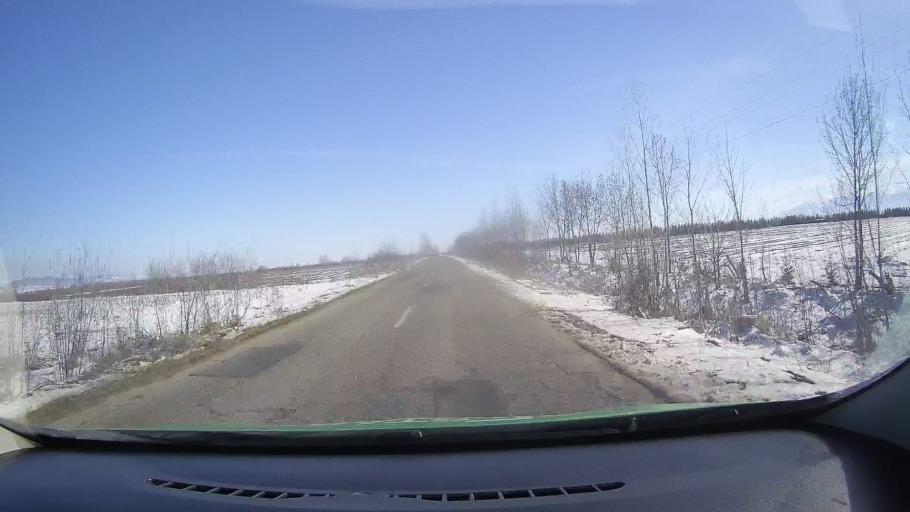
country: RO
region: Brasov
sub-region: Comuna Dragus
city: Dragus
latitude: 45.7541
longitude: 24.7510
